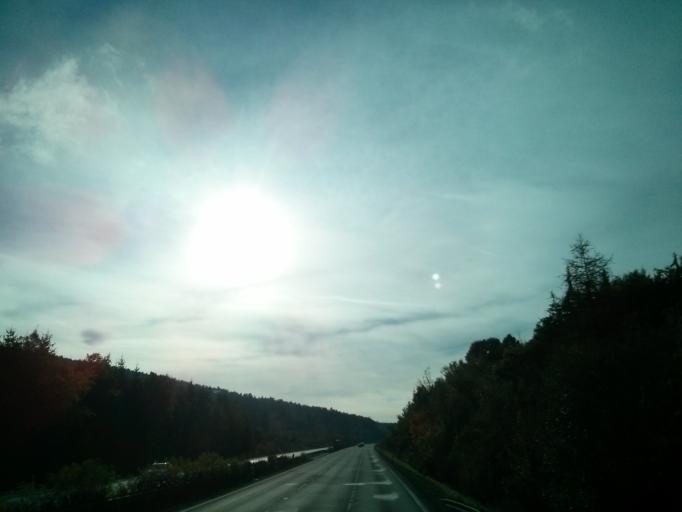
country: CZ
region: Plzensky
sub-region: Okres Rokycany
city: Rokycany
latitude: 49.7455
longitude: 13.5497
